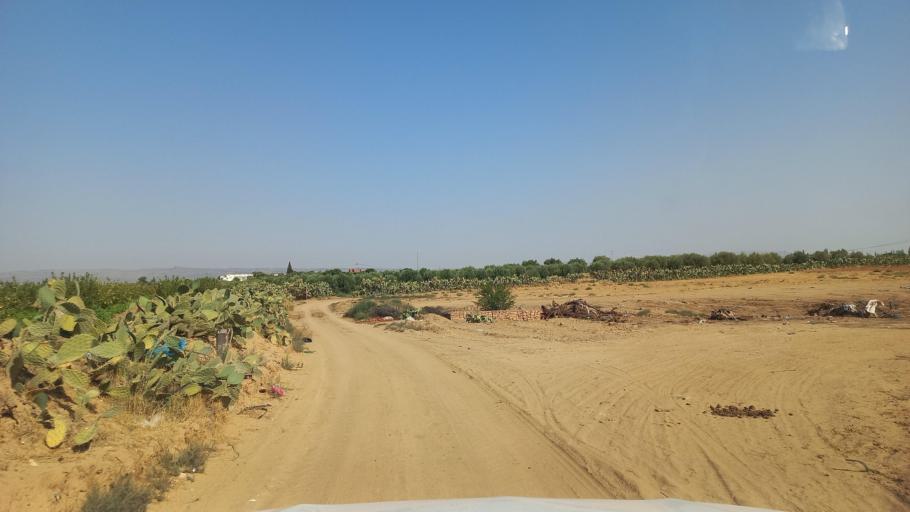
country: TN
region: Al Qasrayn
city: Kasserine
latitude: 35.2481
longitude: 9.0420
